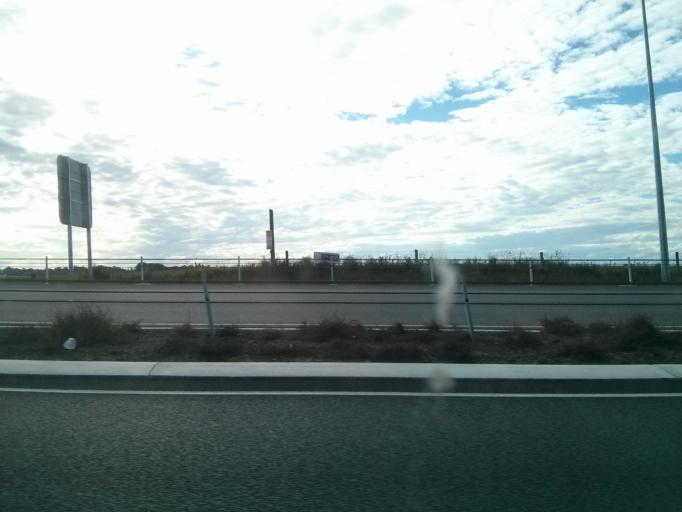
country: NZ
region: Canterbury
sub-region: Christchurch City
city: Christchurch
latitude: -43.4766
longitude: 172.5573
